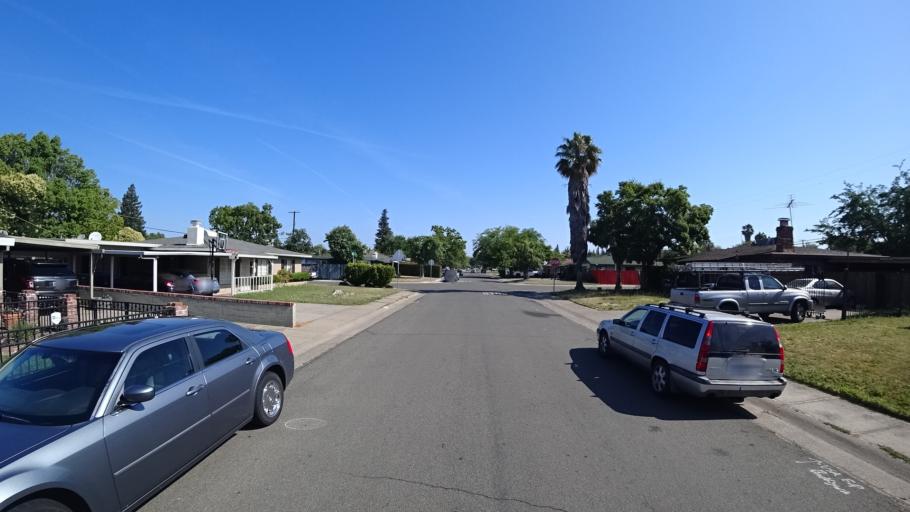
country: US
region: California
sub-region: Sacramento County
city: Florin
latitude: 38.5285
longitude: -121.4329
